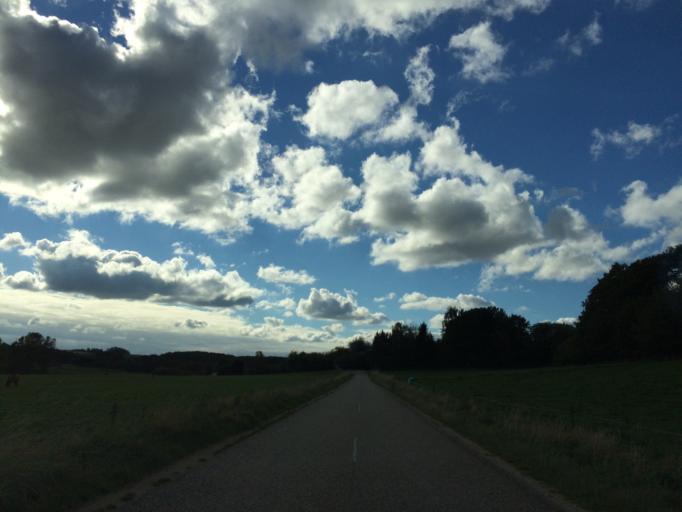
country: DK
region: Central Jutland
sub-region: Skanderborg Kommune
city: Ry
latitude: 56.1615
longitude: 9.7567
